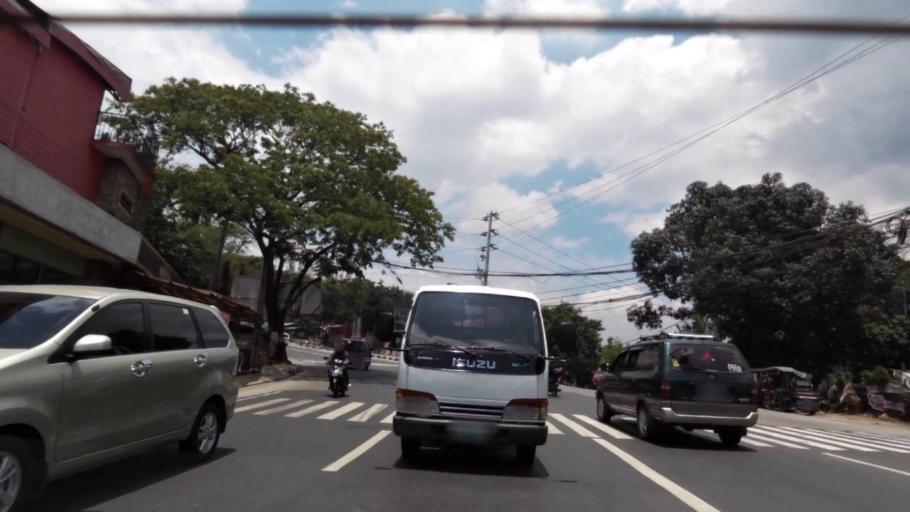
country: PH
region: Calabarzon
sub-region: Province of Rizal
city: Antipolo
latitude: 14.6060
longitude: 121.1735
